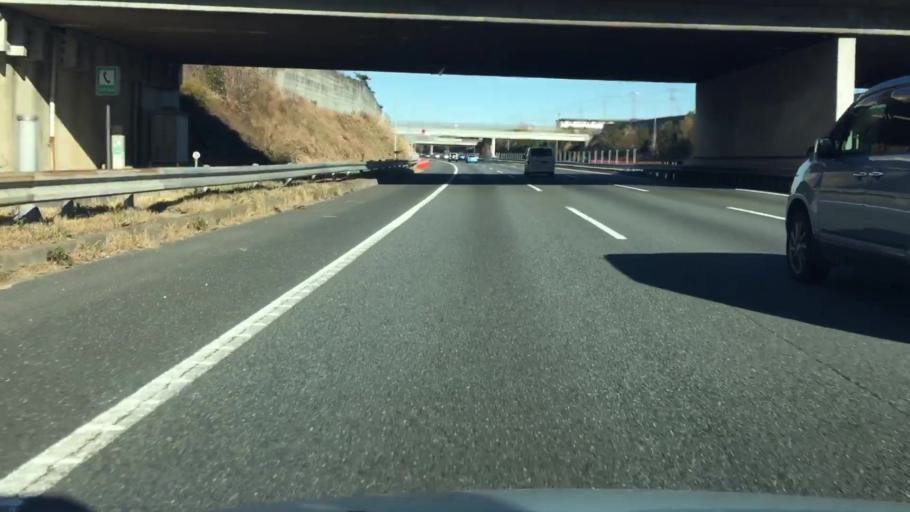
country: JP
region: Saitama
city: Sakado
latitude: 36.0025
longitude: 139.3879
